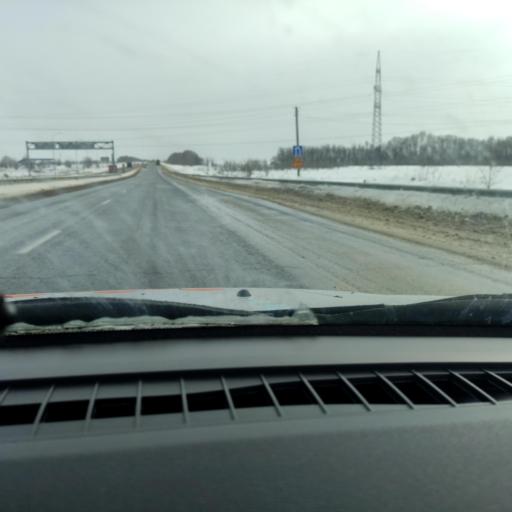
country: RU
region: Samara
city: Dubovyy Umet
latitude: 53.0137
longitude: 50.2380
